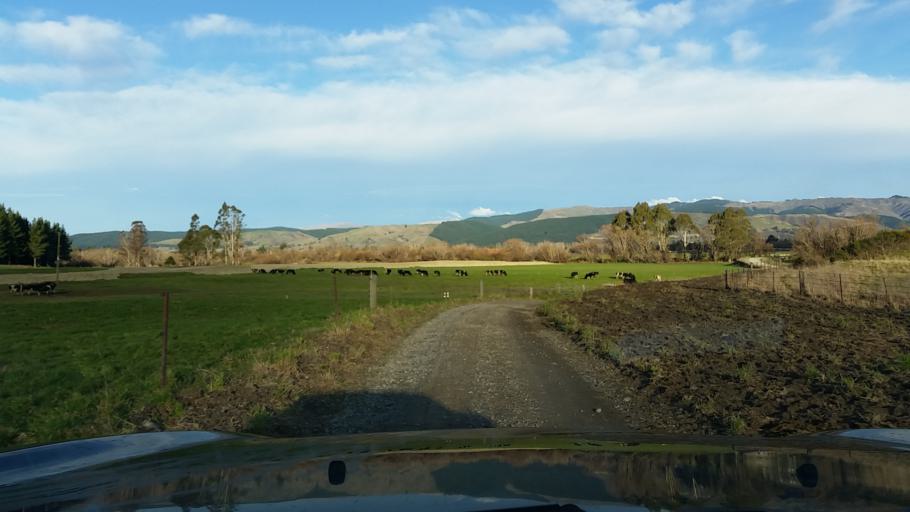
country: NZ
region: Nelson
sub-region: Nelson City
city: Nelson
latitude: -41.5412
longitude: 173.4966
